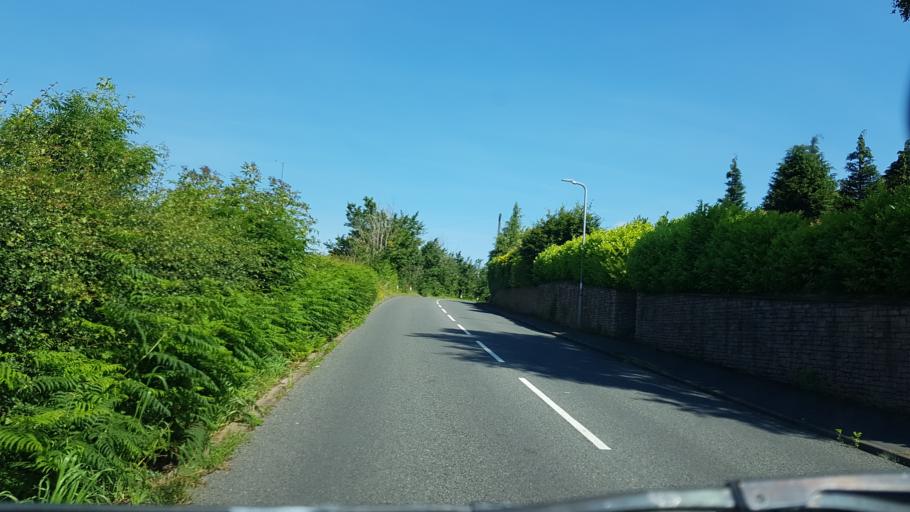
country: GB
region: England
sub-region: Worcestershire
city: Stourport-on-Severn
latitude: 52.3499
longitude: -2.2974
